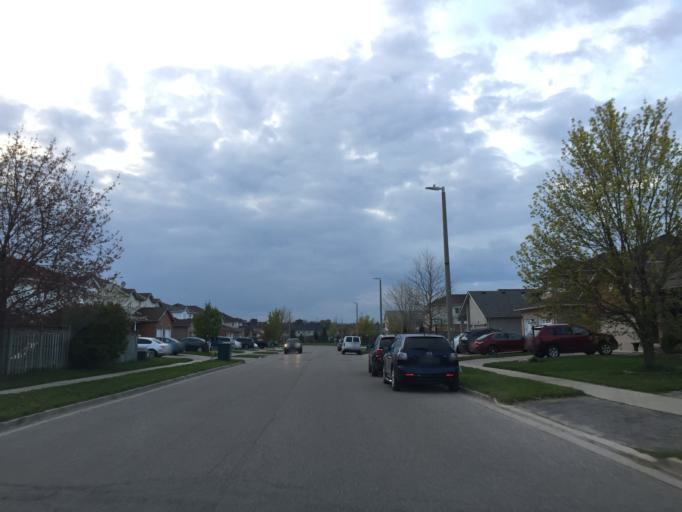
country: CA
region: Ontario
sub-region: Wellington County
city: Guelph
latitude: 43.5268
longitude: -80.2745
